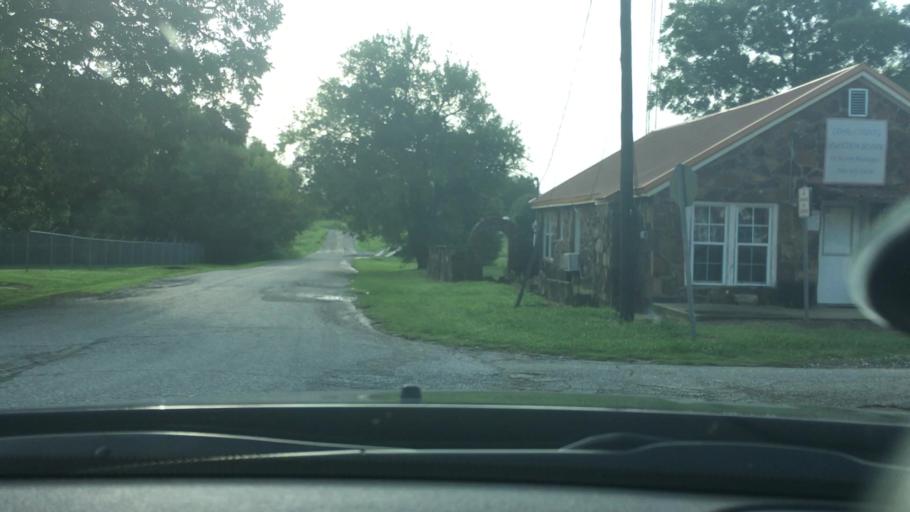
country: US
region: Oklahoma
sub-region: Coal County
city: Coalgate
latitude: 34.5394
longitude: -96.2175
